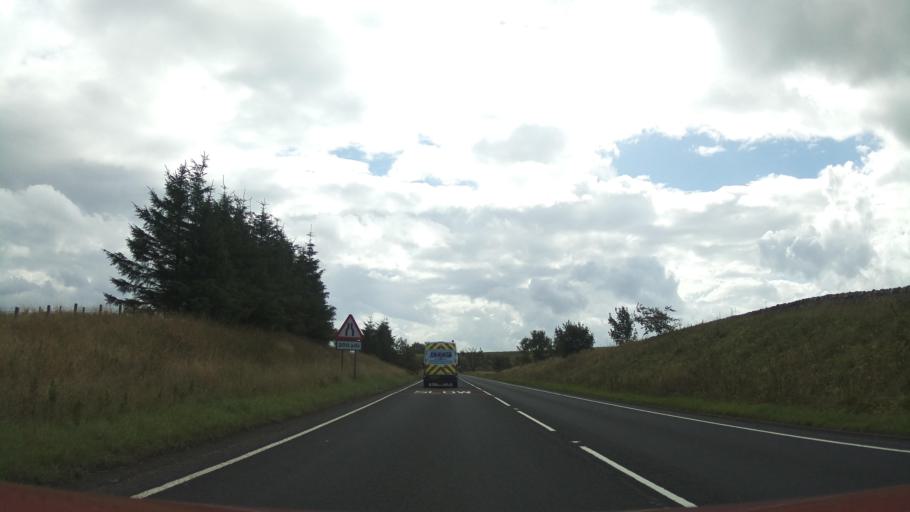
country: GB
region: England
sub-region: Northumberland
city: Birtley
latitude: 55.1260
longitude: -2.1433
